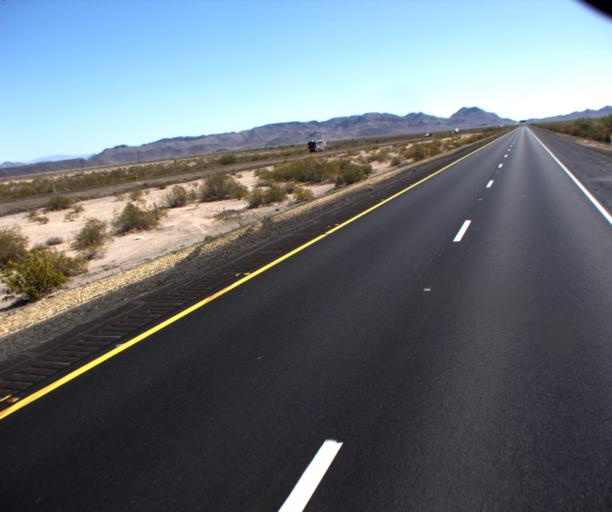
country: US
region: Arizona
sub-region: La Paz County
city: Salome
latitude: 33.6221
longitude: -113.7094
